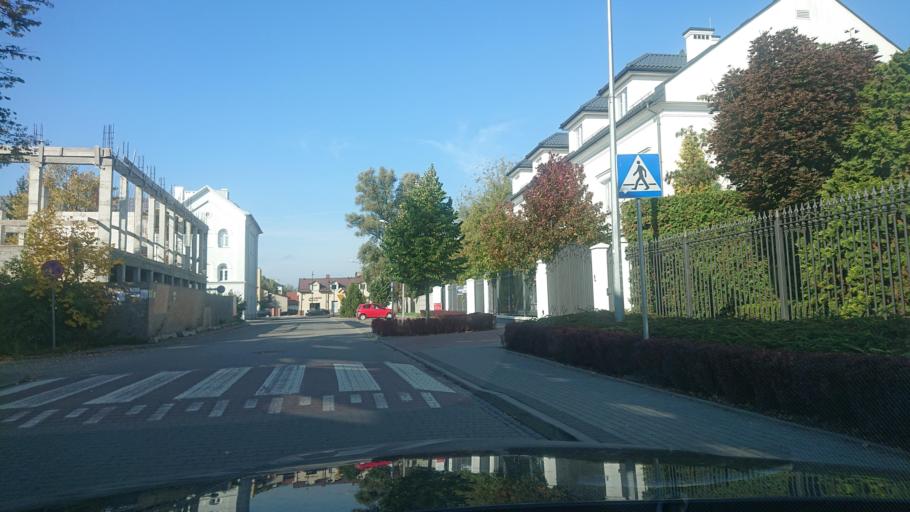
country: PL
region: Masovian Voivodeship
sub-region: Powiat piaseczynski
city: Gora Kalwaria
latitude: 51.9796
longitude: 21.2177
